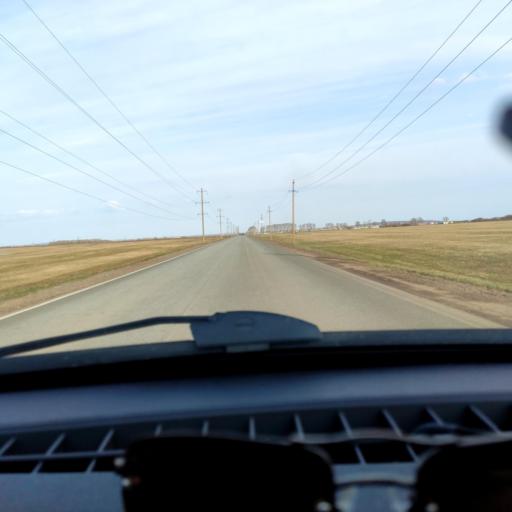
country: RU
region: Bashkortostan
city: Kabakovo
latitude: 54.5401
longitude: 56.0614
